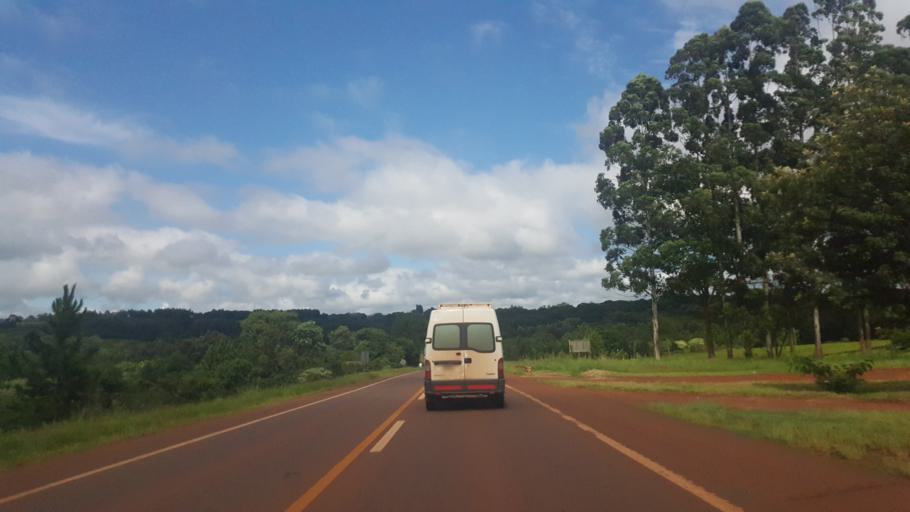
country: AR
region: Misiones
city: Aristobulo del Valle
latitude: -27.0851
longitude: -54.8407
